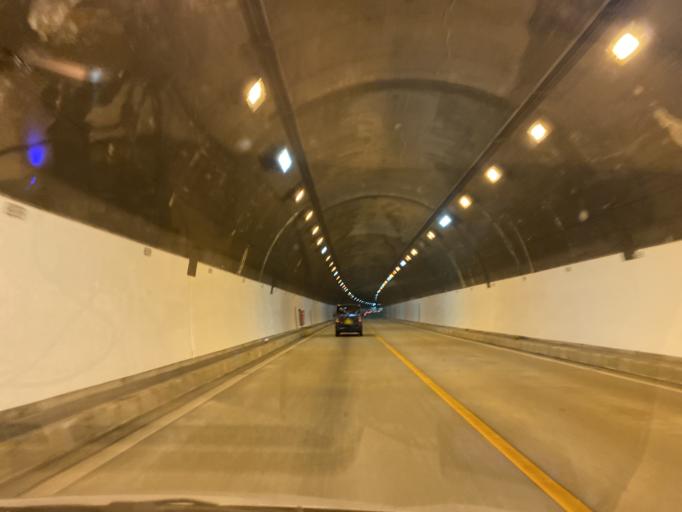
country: JP
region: Wakayama
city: Iwade
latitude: 34.3507
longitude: 135.2871
